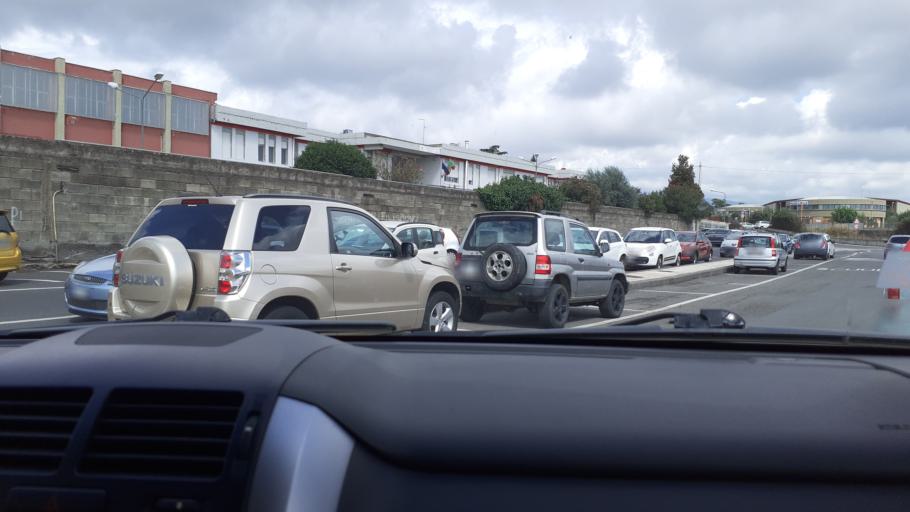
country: IT
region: Sicily
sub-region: Catania
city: San Giovanni la Punta
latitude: 37.5785
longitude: 15.1013
